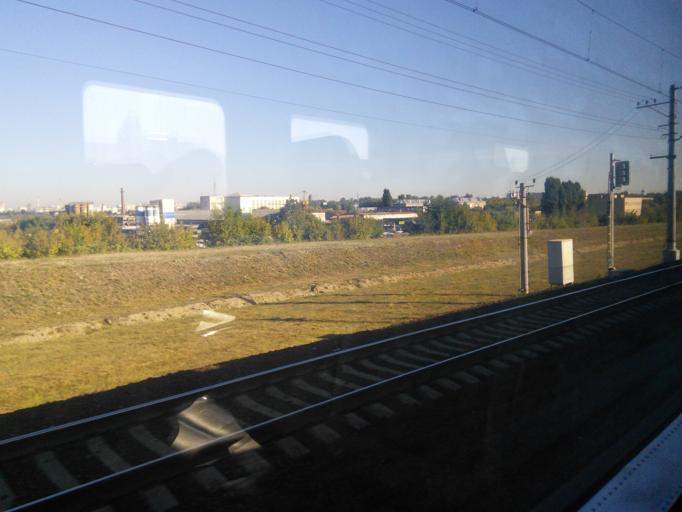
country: RU
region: Moskovskaya
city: Kur'yanovo
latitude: 55.6469
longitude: 37.6964
